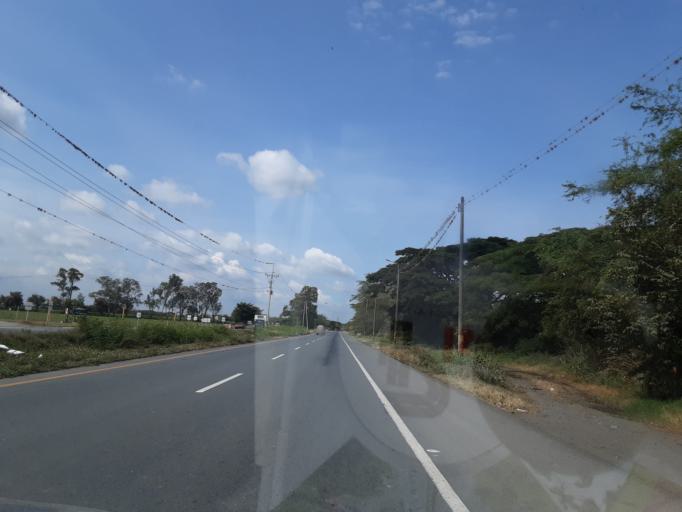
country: CO
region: Valle del Cauca
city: Guacari
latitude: 3.7754
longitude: -76.3263
